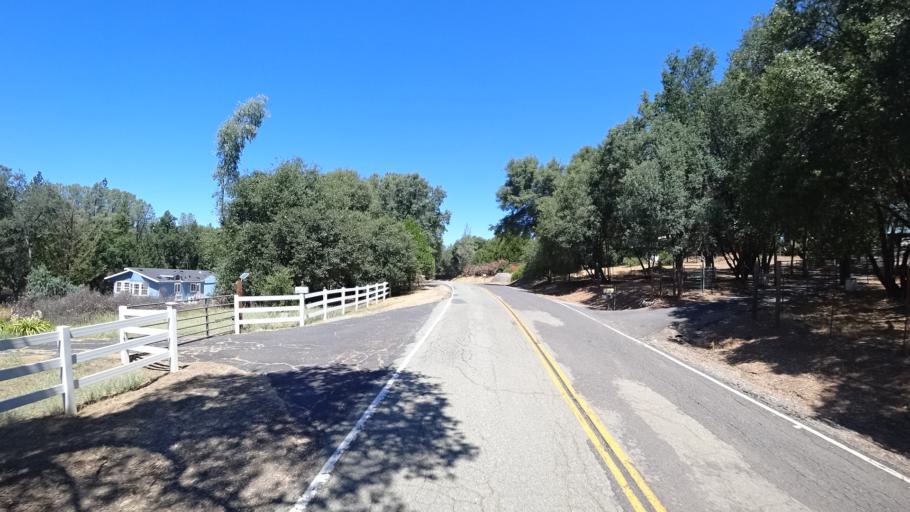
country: US
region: California
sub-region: Calaveras County
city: Mountain Ranch
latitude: 38.2116
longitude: -120.5292
